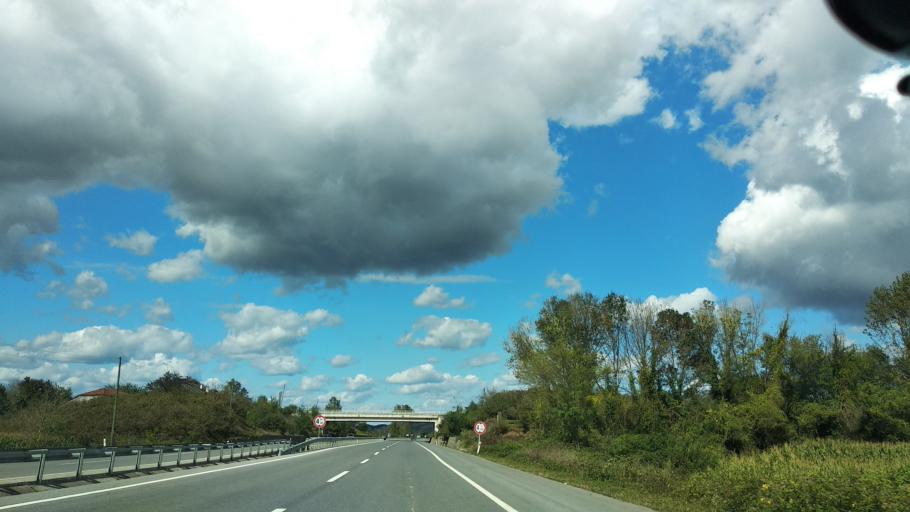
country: TR
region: Sakarya
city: Ortakoy
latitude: 41.0216
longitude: 30.6139
